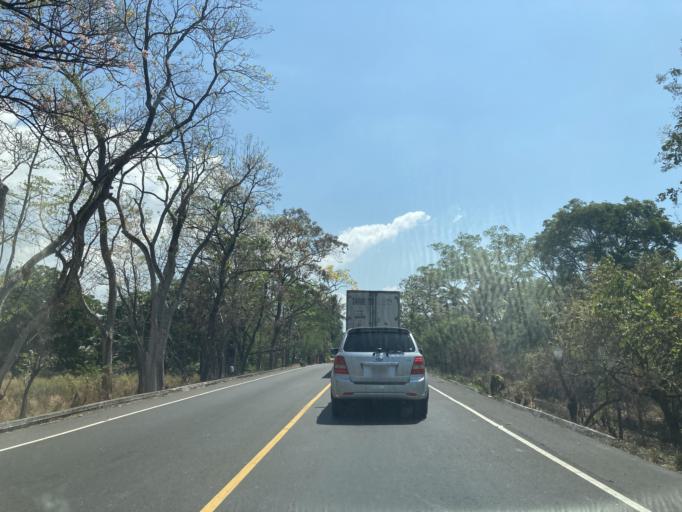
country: GT
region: Santa Rosa
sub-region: Municipio de Taxisco
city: Taxisco
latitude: 14.0949
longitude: -90.5725
